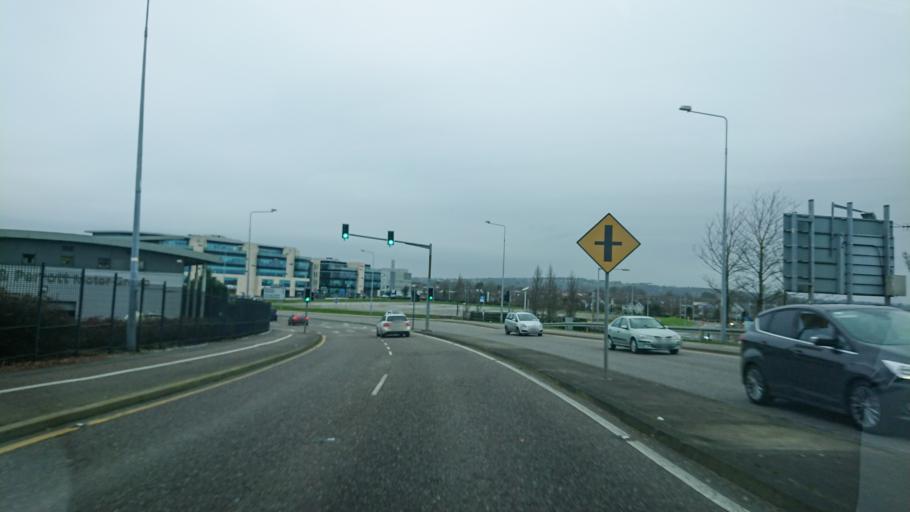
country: IE
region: Munster
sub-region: County Cork
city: Passage West
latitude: 51.8848
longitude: -8.3988
